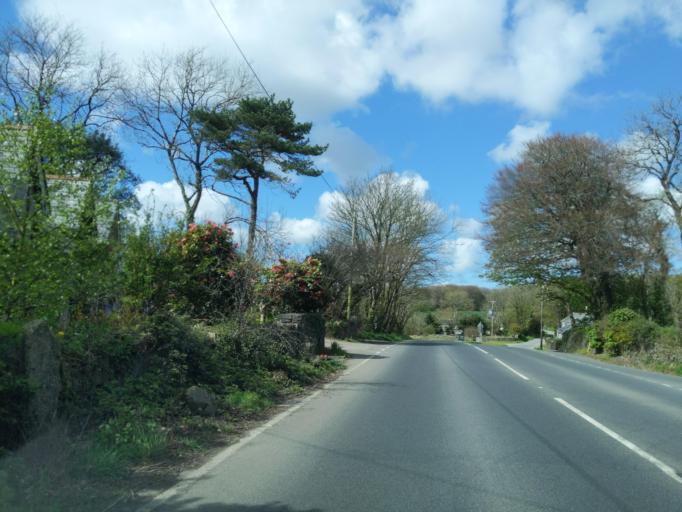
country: GB
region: England
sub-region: Cornwall
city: Bodmin
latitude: 50.4938
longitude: -4.7679
